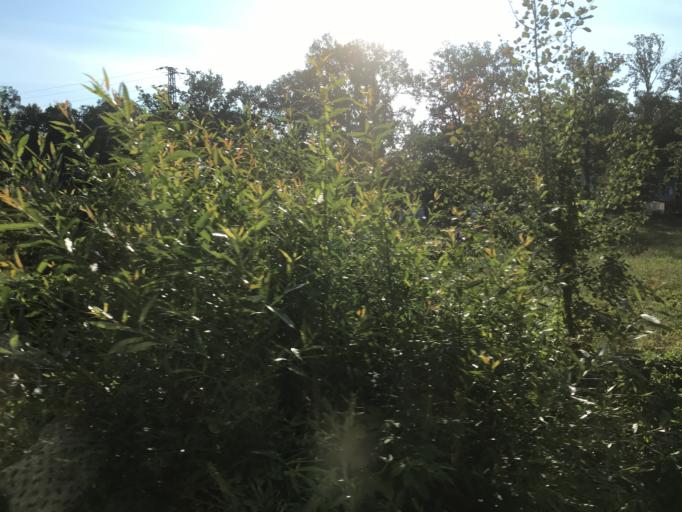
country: CZ
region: Jihocesky
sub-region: Okres Jindrichuv Hradec
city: Trebon
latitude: 49.0335
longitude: 14.7511
